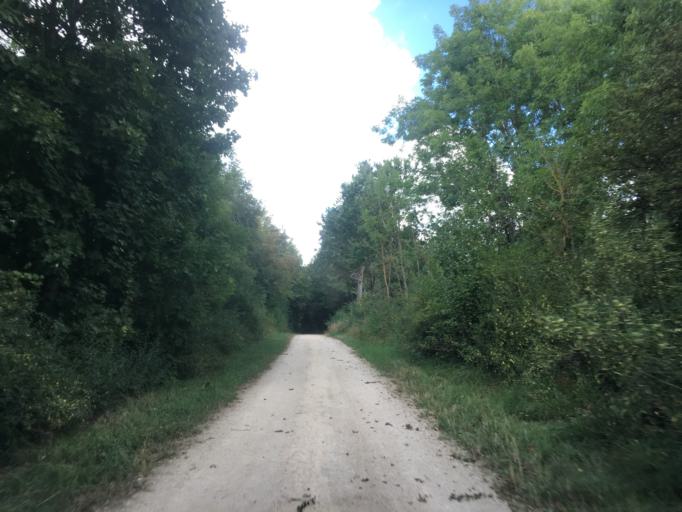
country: DE
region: Baden-Wuerttemberg
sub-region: Tuebingen Region
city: Hayingen
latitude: 48.2761
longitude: 9.5015
